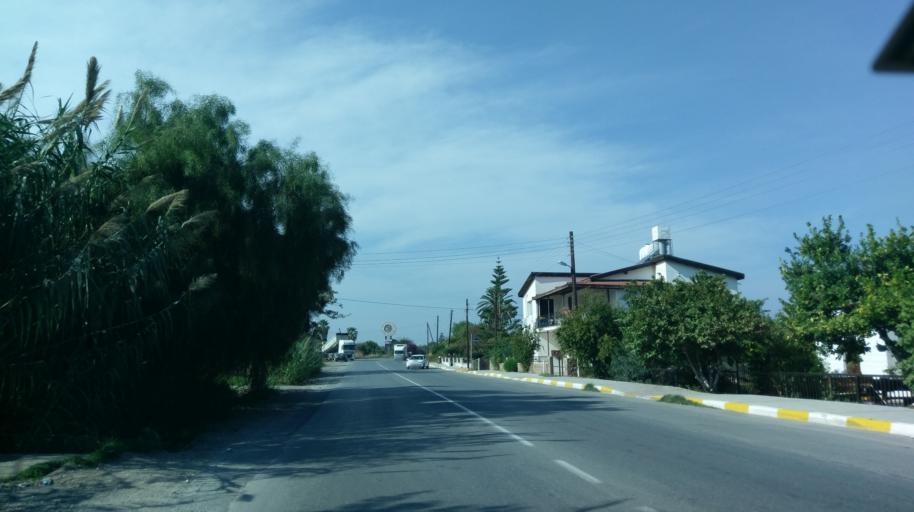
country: CY
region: Keryneia
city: Kyrenia
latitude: 35.3436
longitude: 33.2627
